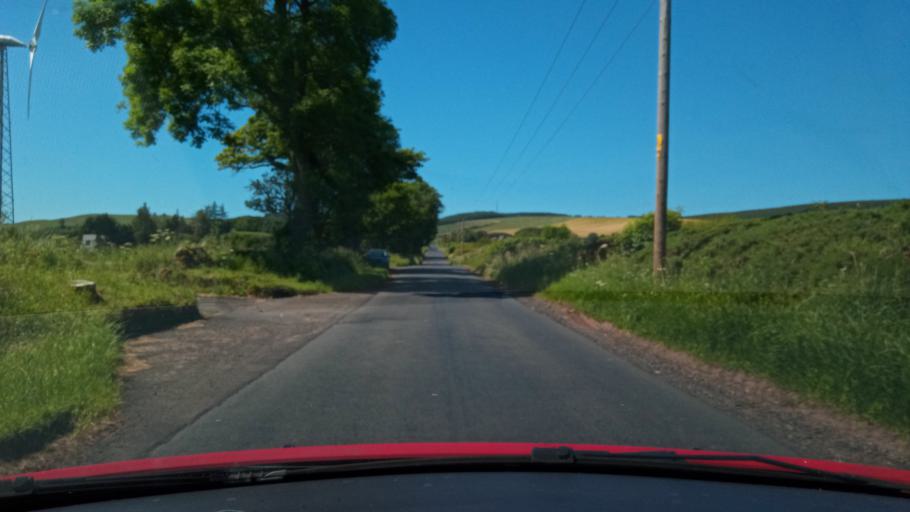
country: GB
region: Scotland
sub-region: The Scottish Borders
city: Duns
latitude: 55.7777
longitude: -2.3837
